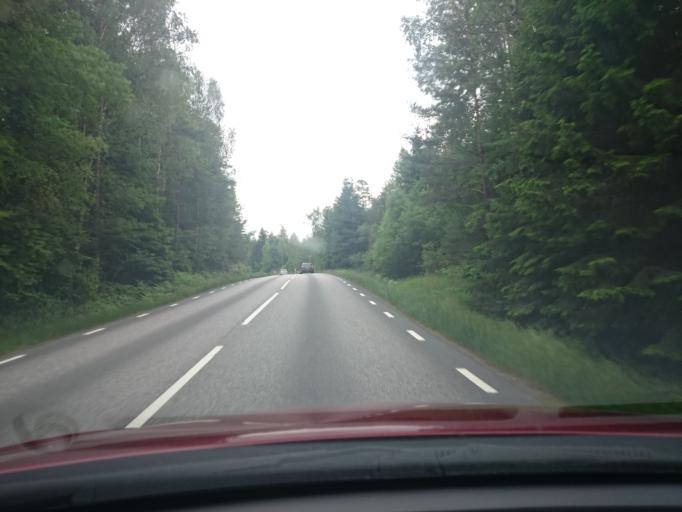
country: SE
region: Vaestra Goetaland
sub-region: Lerums Kommun
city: Stenkullen
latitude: 57.7554
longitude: 12.3214
